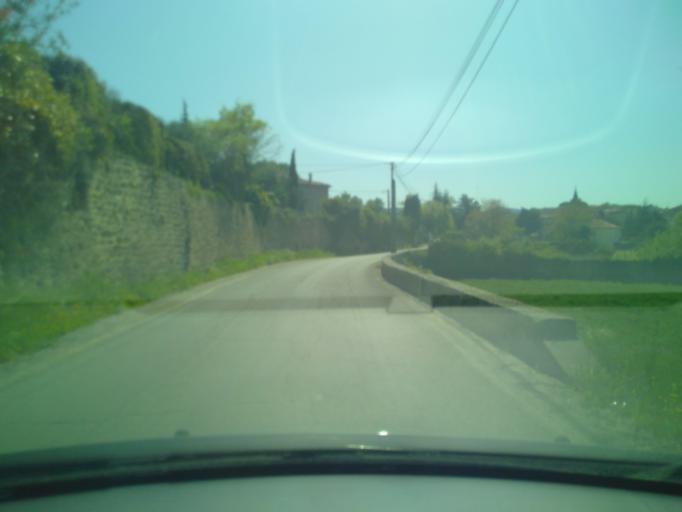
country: FR
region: Provence-Alpes-Cote d'Azur
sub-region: Departement du Vaucluse
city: Malemort-du-Comtat
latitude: 44.0244
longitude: 5.1573
